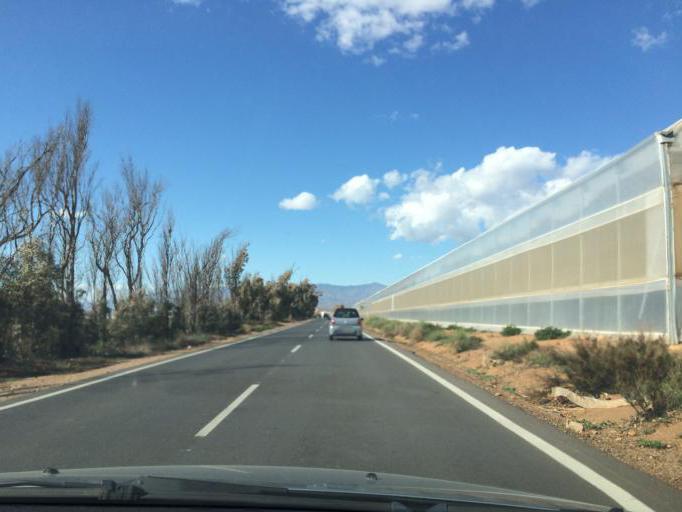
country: ES
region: Andalusia
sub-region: Provincia de Almeria
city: Retamar
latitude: 36.7895
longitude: -2.2284
